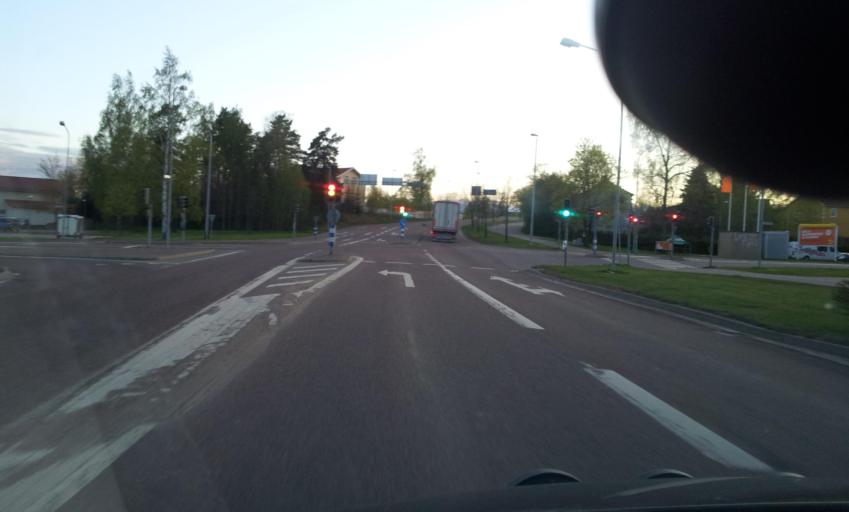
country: SE
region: Gaevleborg
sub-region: Bollnas Kommun
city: Bollnas
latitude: 61.3561
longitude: 16.4002
